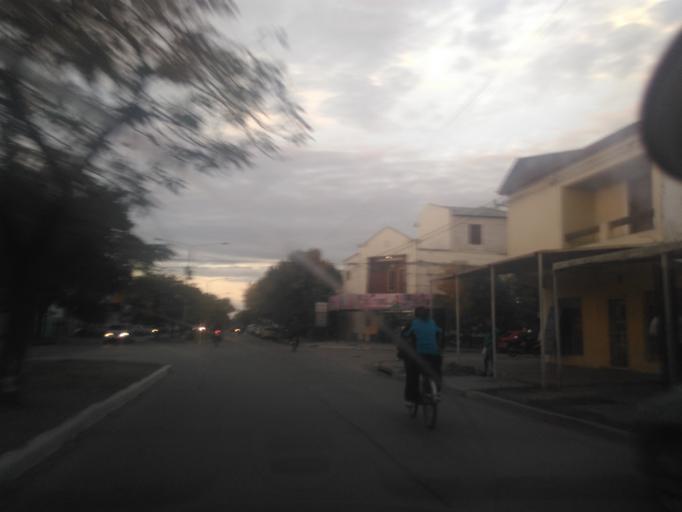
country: AR
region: Chaco
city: Resistencia
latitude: -27.4666
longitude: -58.9949
